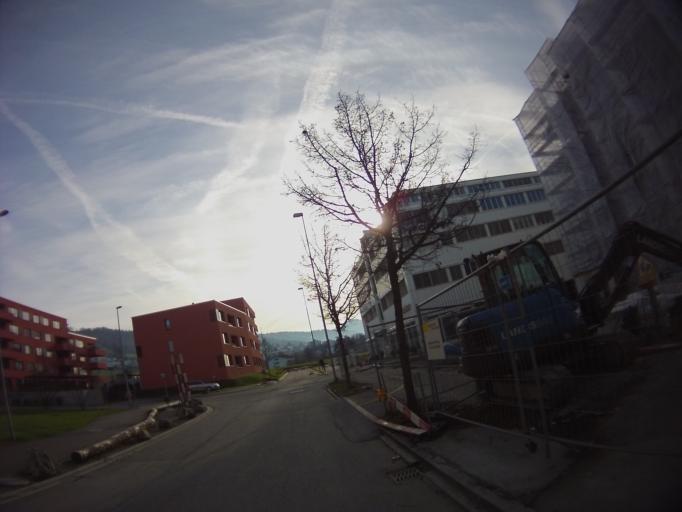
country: CH
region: Zug
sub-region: Zug
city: Zug
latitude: 47.1803
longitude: 8.5258
